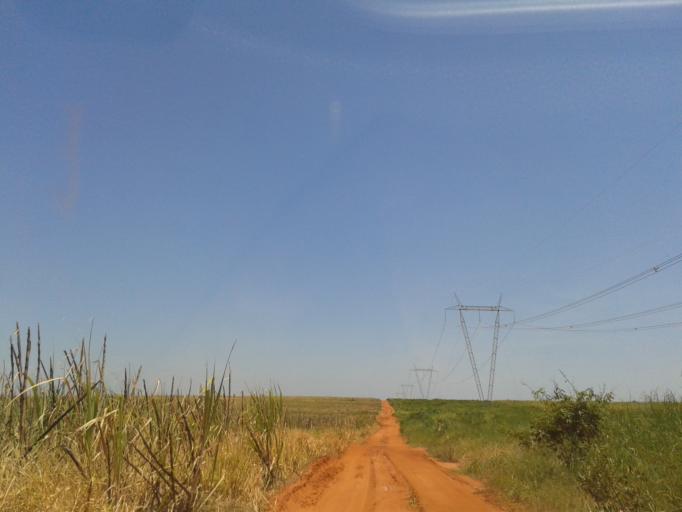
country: BR
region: Minas Gerais
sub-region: Santa Vitoria
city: Santa Vitoria
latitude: -19.0827
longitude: -50.4557
